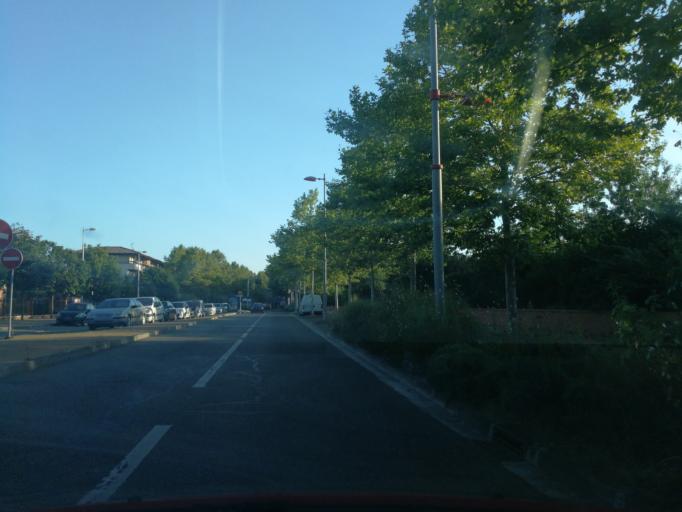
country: FR
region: Midi-Pyrenees
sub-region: Departement de la Haute-Garonne
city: Toulouse
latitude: 43.6300
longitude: 1.4496
